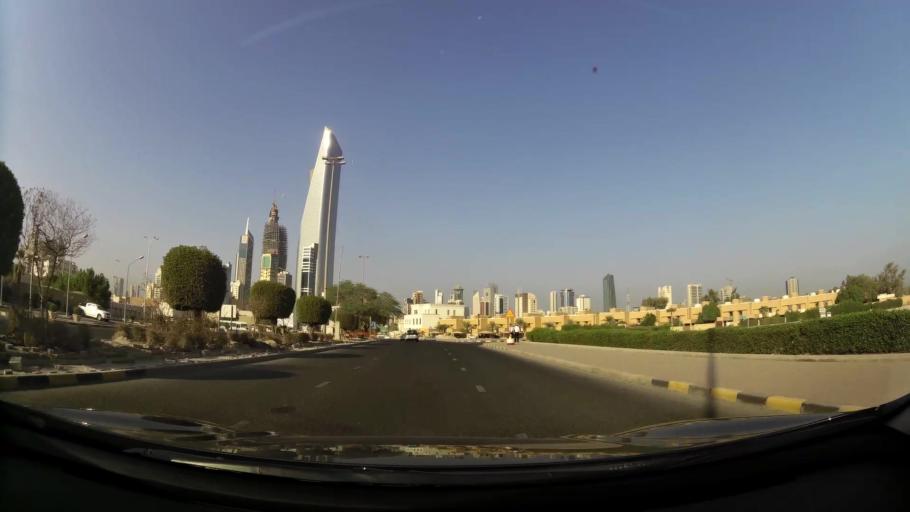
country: KW
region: Al Asimah
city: Ad Dasmah
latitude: 29.3822
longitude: 48.0013
